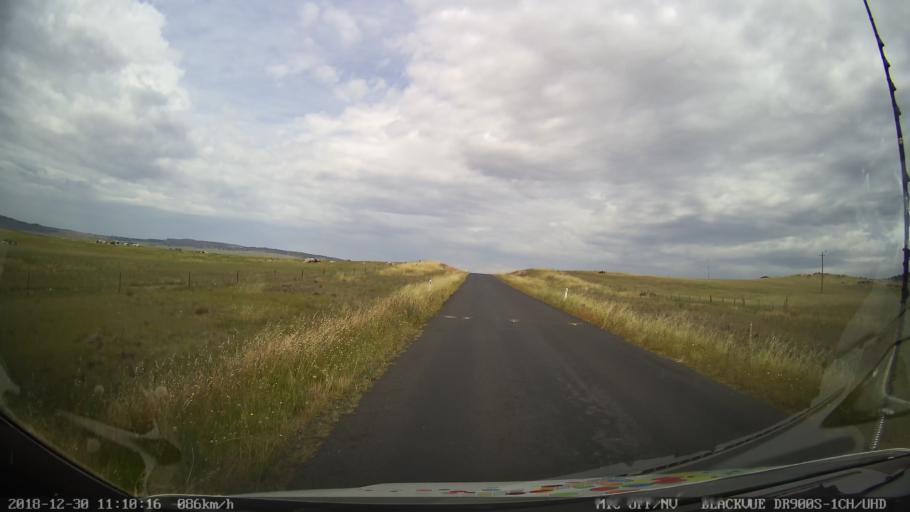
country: AU
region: New South Wales
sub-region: Snowy River
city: Berridale
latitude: -36.5133
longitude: 148.7834
